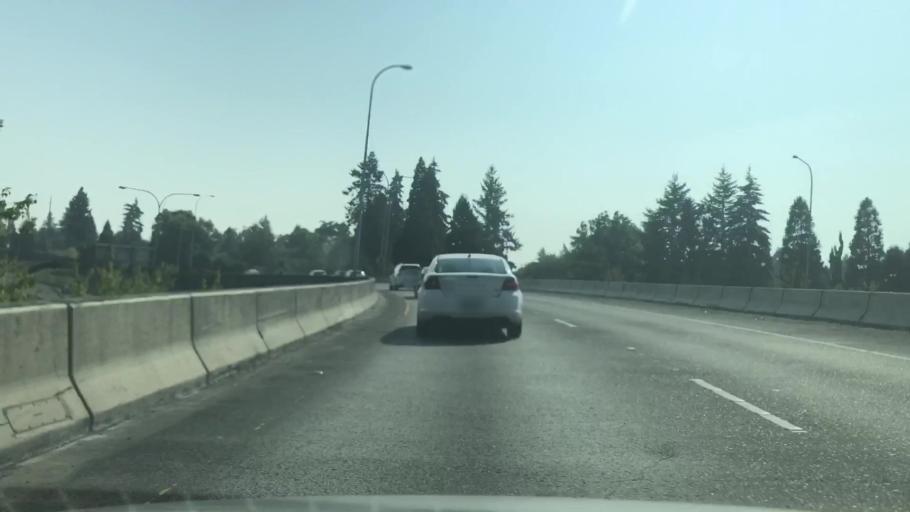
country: US
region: Washington
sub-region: Clark County
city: Vancouver
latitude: 45.6493
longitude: -122.6600
